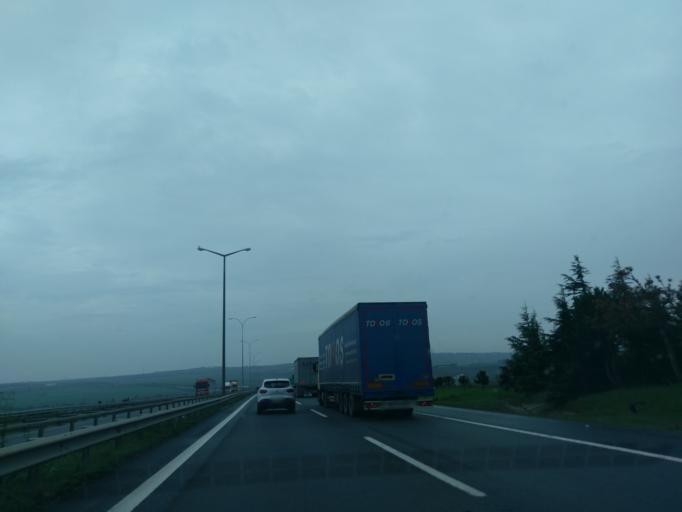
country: TR
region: Istanbul
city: Silivri
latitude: 41.1146
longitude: 28.2595
